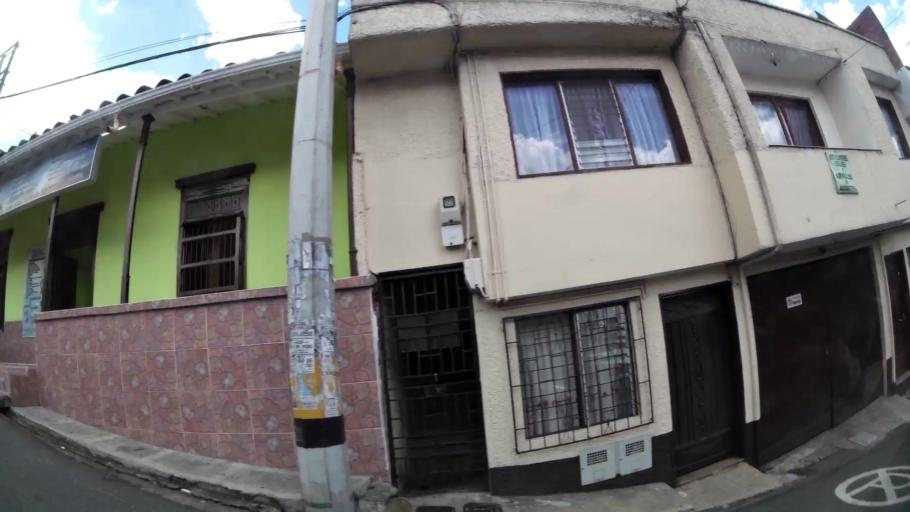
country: CO
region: Antioquia
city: La Estrella
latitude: 6.1568
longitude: -75.6448
